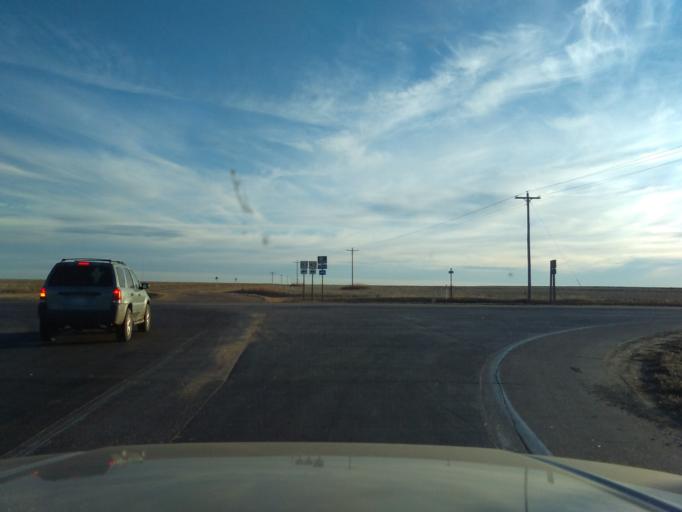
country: US
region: Kansas
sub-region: Logan County
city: Oakley
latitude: 39.1195
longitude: -100.8682
